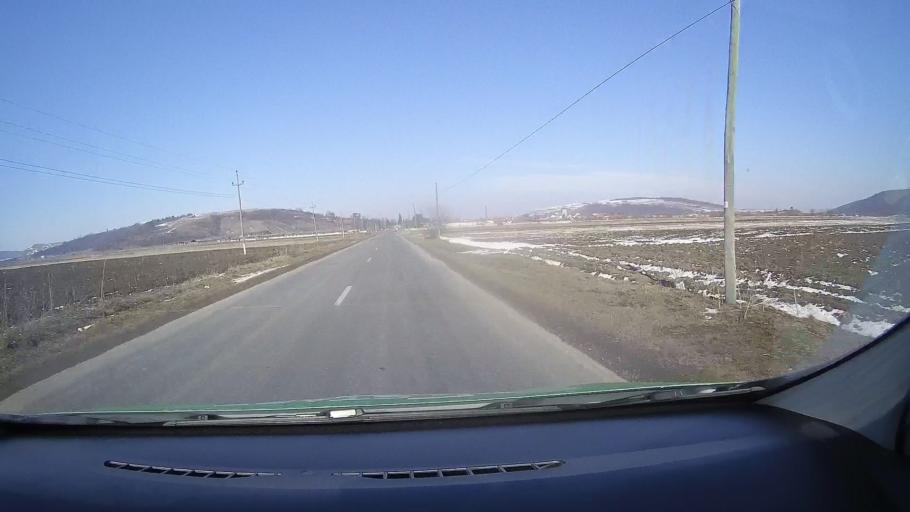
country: RO
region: Brasov
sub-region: Comuna Homorod
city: Homorod
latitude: 46.0300
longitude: 25.2738
